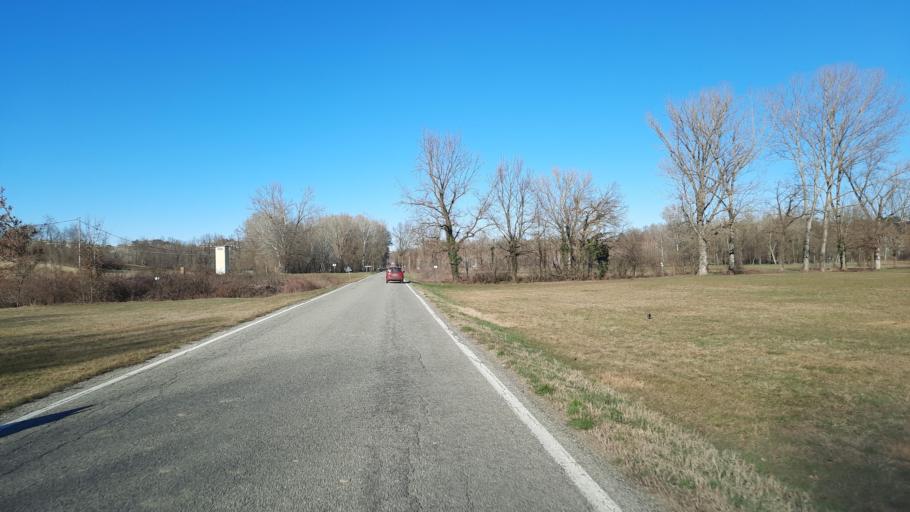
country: IT
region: Piedmont
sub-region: Provincia di Alessandria
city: Frassinello Monferrato
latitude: 45.0492
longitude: 8.3935
